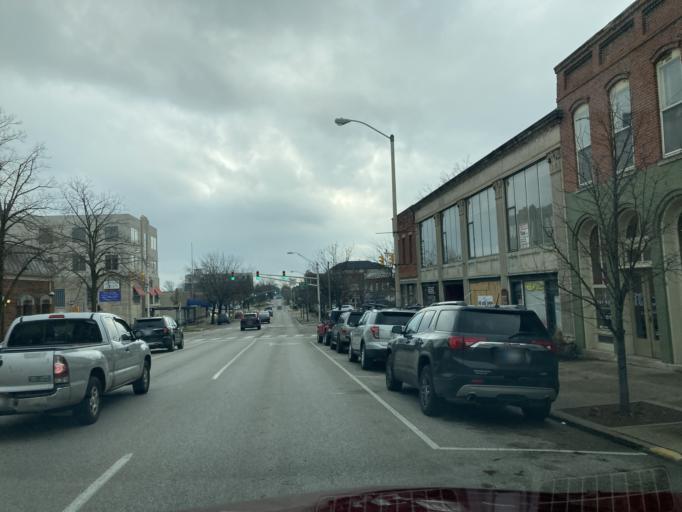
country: US
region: Indiana
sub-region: Monroe County
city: Bloomington
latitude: 39.1661
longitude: -86.5349
